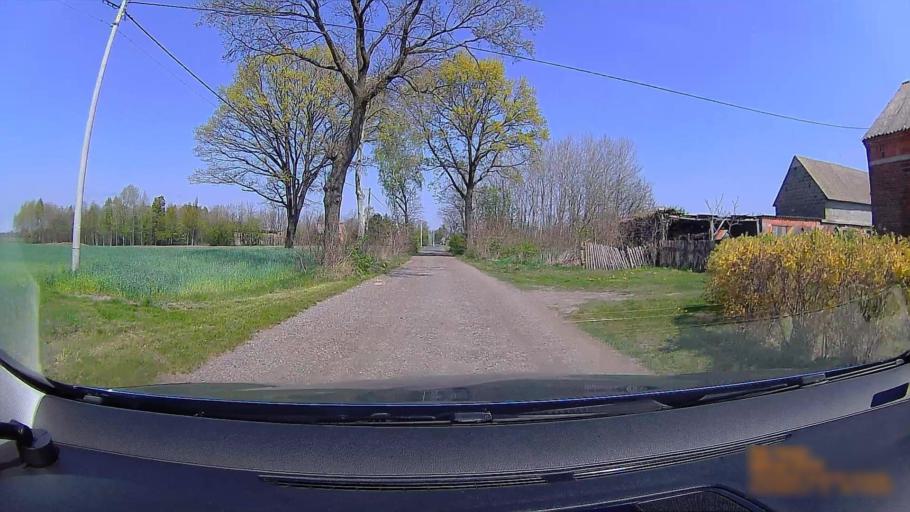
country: PL
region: Greater Poland Voivodeship
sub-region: Powiat koninski
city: Rychwal
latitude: 52.0948
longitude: 18.1834
